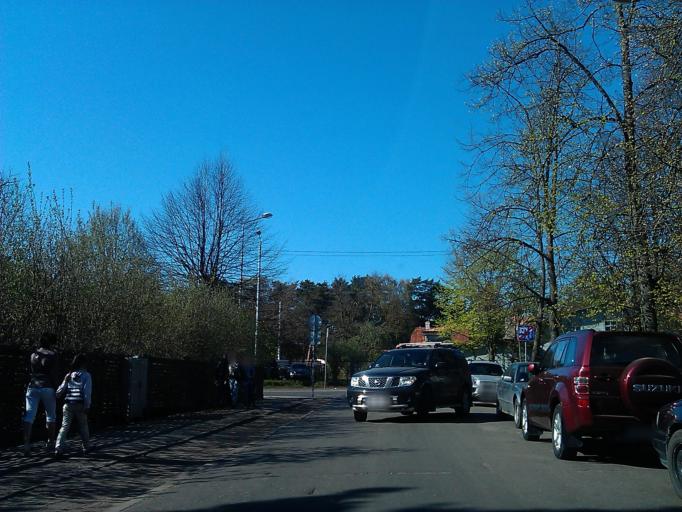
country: LV
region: Riga
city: Jaunciems
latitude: 57.0060
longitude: 24.1601
